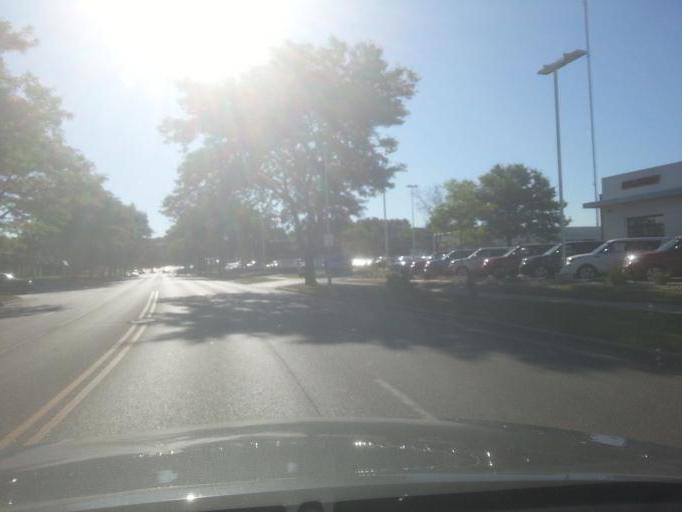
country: US
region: Wisconsin
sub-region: Dane County
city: Middleton
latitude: 43.0550
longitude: -89.4937
